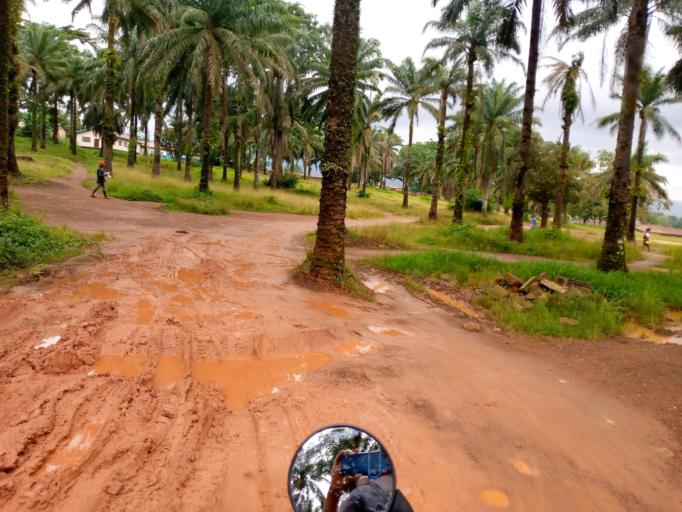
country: SL
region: Eastern Province
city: Kenema
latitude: 7.8644
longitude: -11.1848
